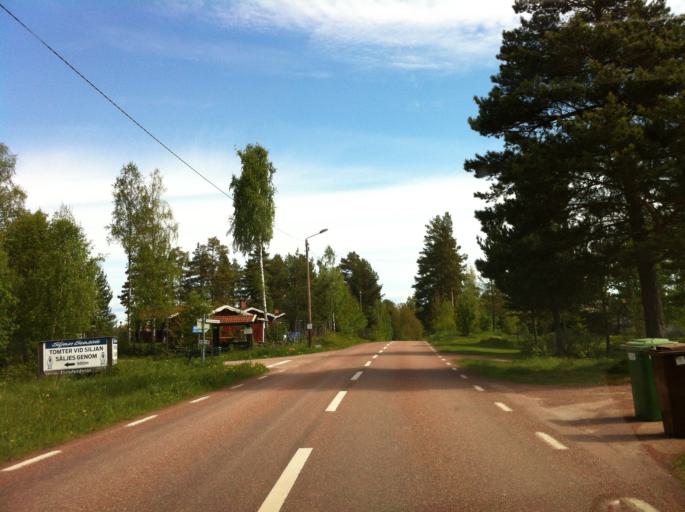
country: SE
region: Dalarna
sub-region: Mora Kommun
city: Mora
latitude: 60.8907
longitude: 14.5467
